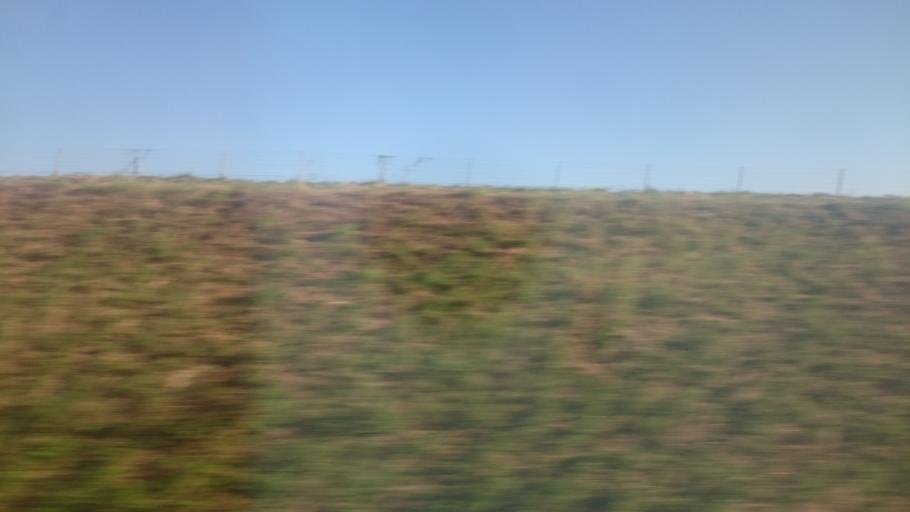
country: FR
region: Centre
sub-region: Departement du Loir-et-Cher
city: Mondoubleau
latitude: 48.0851
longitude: 0.8736
